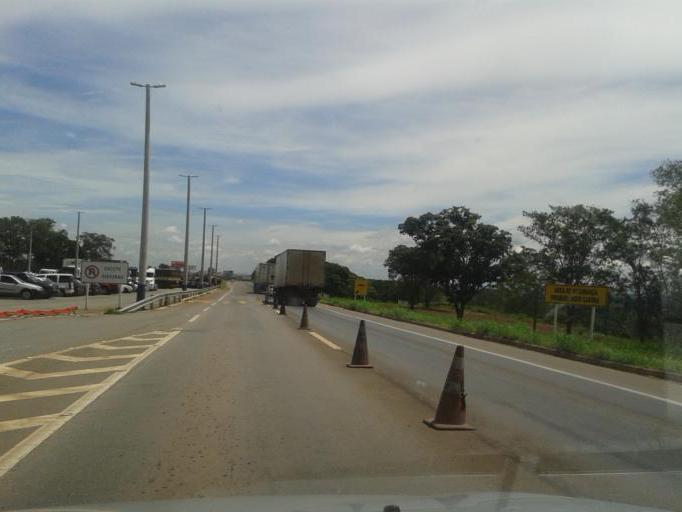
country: BR
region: Goias
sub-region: Hidrolandia
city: Hidrolandia
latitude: -16.9217
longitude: -49.2524
